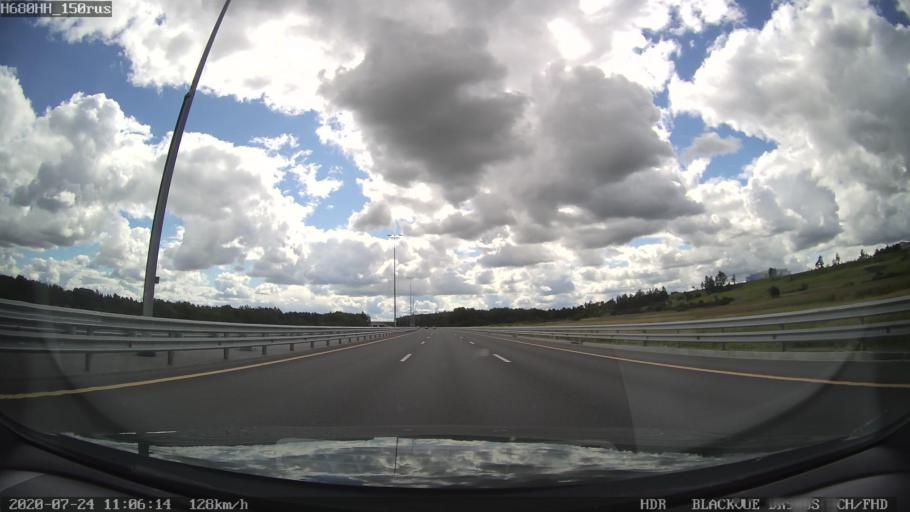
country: RU
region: St.-Petersburg
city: Shushary
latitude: 59.7661
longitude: 30.3697
